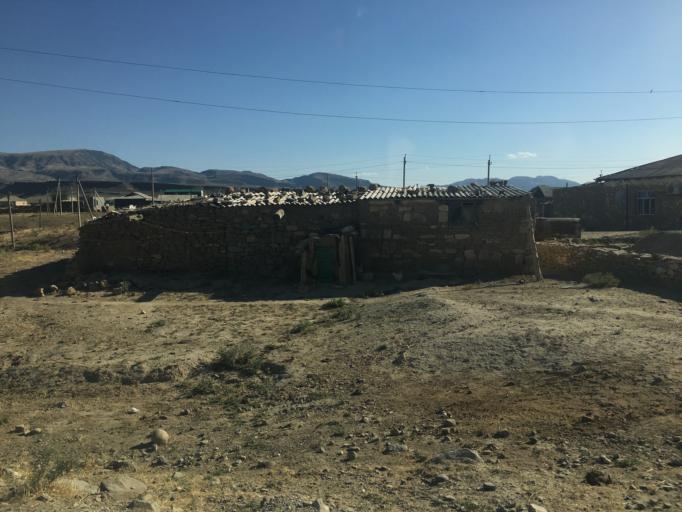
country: TM
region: Balkan
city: Magtymguly
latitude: 38.6355
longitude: 56.6047
